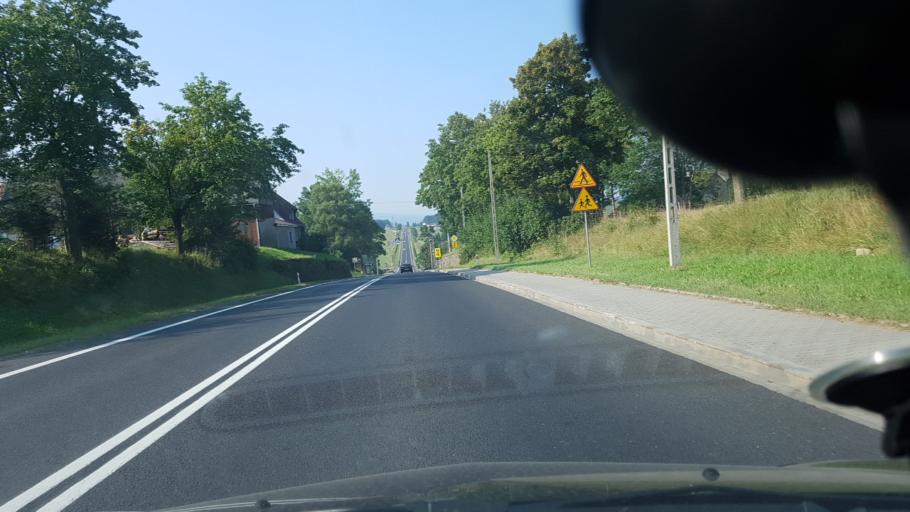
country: PL
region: Lesser Poland Voivodeship
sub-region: Powiat nowotarski
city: Chyzne
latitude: 49.4270
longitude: 19.6747
